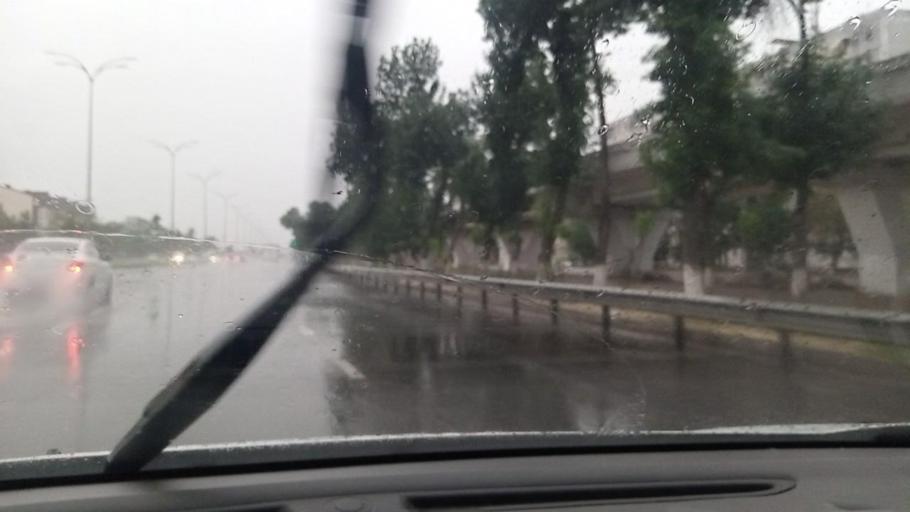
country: UZ
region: Toshkent Shahri
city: Bektemir
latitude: 41.2883
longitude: 69.3595
